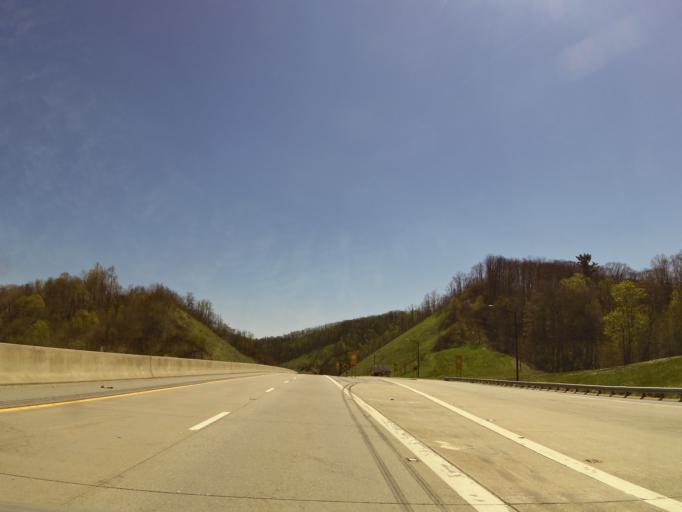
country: US
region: North Carolina
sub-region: Madison County
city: Mars Hill
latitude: 35.9529
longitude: -82.5615
